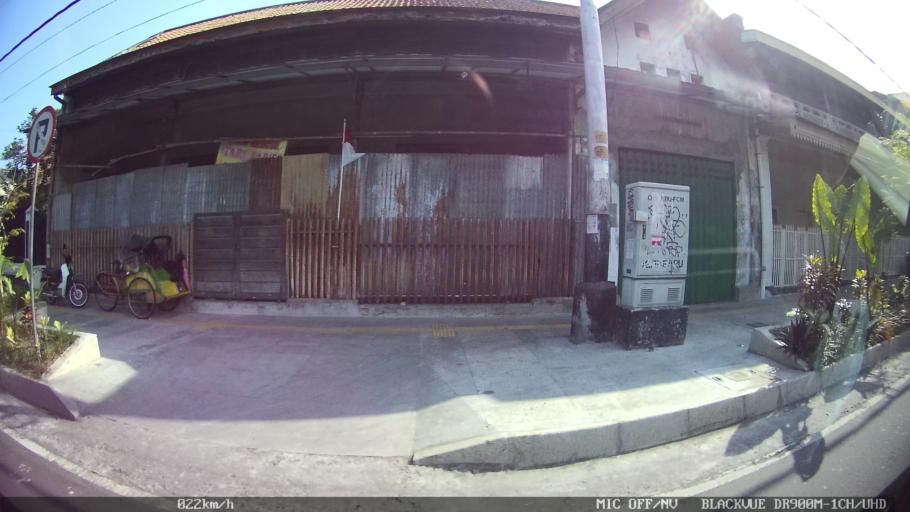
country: ID
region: Daerah Istimewa Yogyakarta
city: Yogyakarta
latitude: -7.8012
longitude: 110.3602
